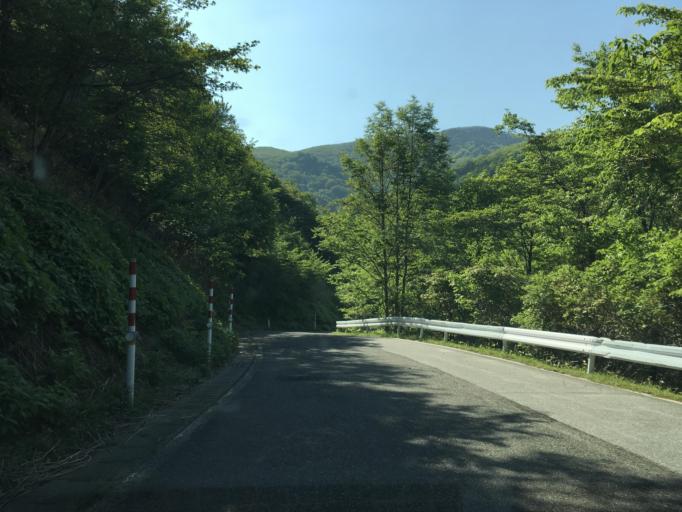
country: JP
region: Iwate
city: Ofunato
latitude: 39.1847
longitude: 141.7459
